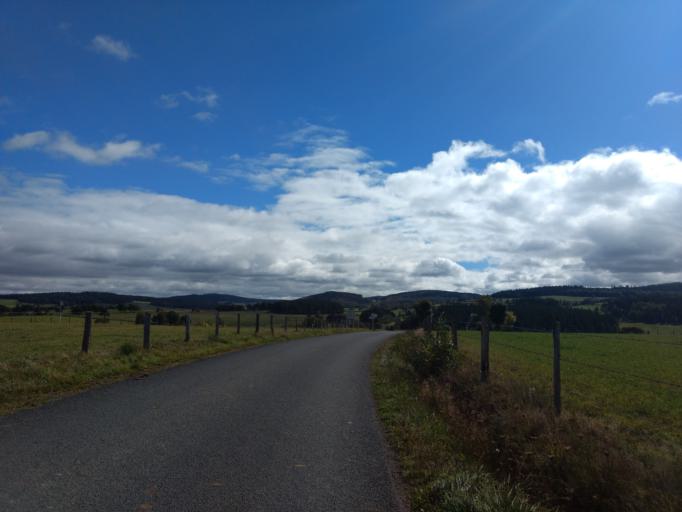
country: FR
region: Auvergne
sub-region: Departement du Cantal
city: Chaudes-Aigues
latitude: 44.8353
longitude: 2.9904
